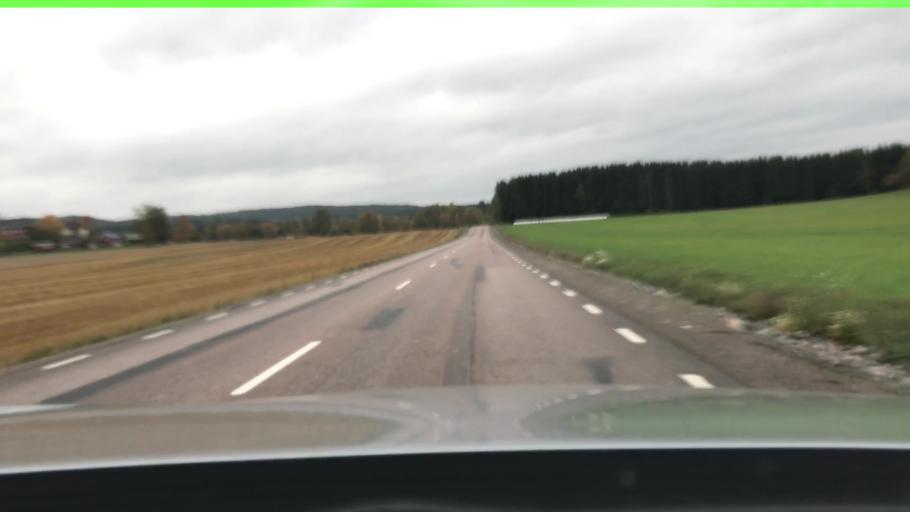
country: SE
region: Vaermland
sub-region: Eda Kommun
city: Amotfors
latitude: 59.7358
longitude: 12.1985
